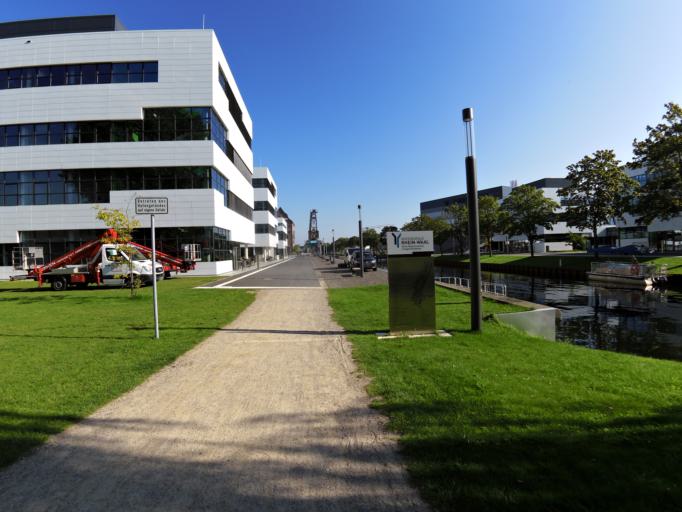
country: DE
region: North Rhine-Westphalia
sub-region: Regierungsbezirk Dusseldorf
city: Kleve
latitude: 51.7927
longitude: 6.1418
